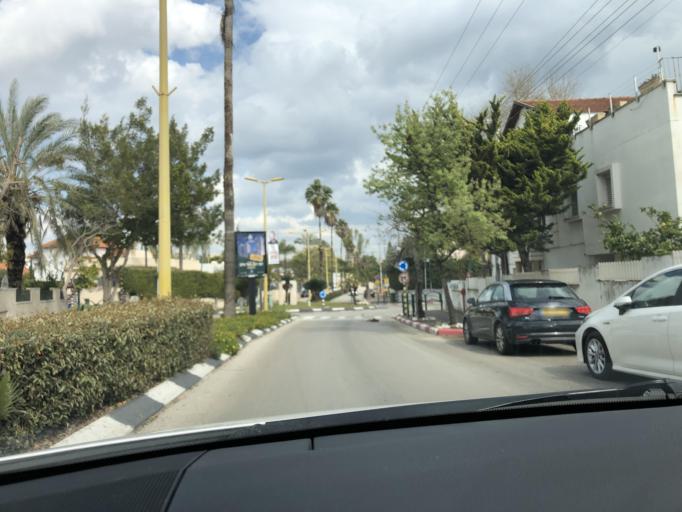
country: IL
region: Central District
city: Ganne Tiqwa
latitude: 32.0575
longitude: 34.8737
